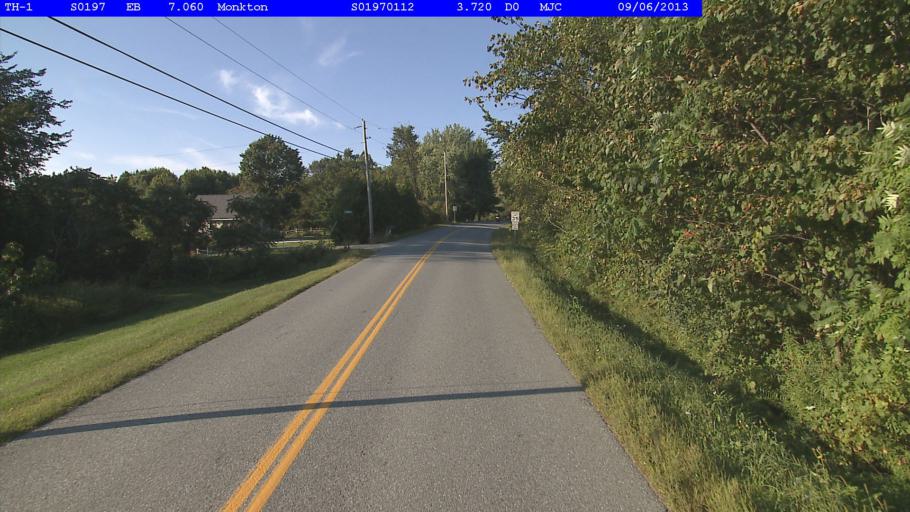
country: US
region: Vermont
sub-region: Chittenden County
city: Hinesburg
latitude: 44.2305
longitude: -73.1515
